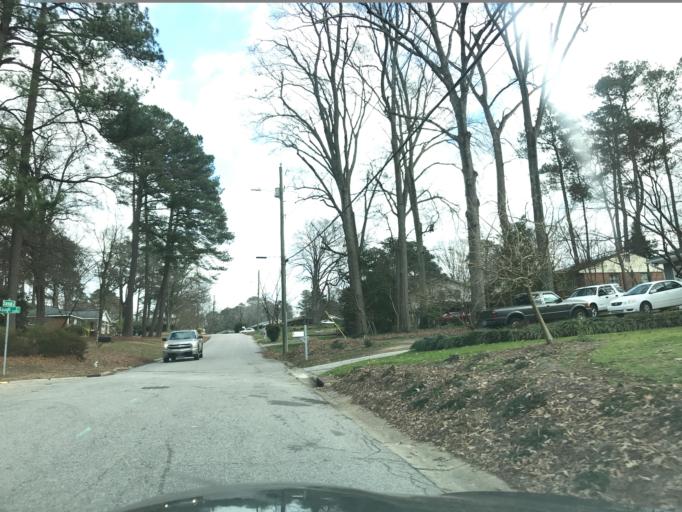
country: US
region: North Carolina
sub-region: Wake County
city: Raleigh
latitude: 35.8232
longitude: -78.5837
